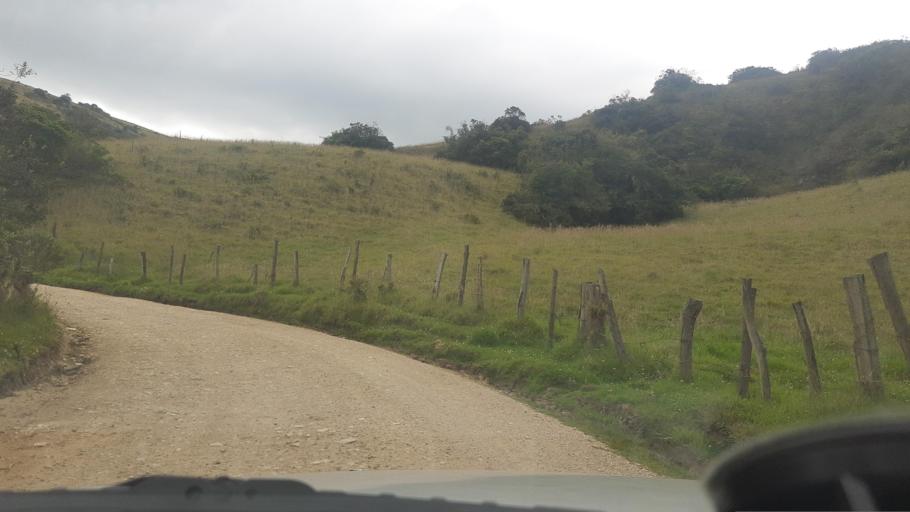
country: CO
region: Cundinamarca
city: Suesca
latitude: 5.1319
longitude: -73.7873
